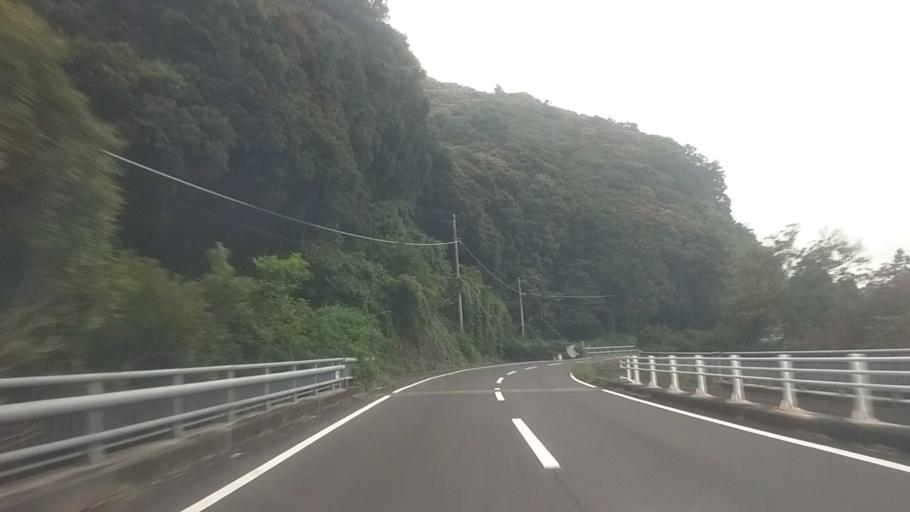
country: JP
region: Chiba
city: Kawaguchi
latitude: 35.1417
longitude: 140.1497
